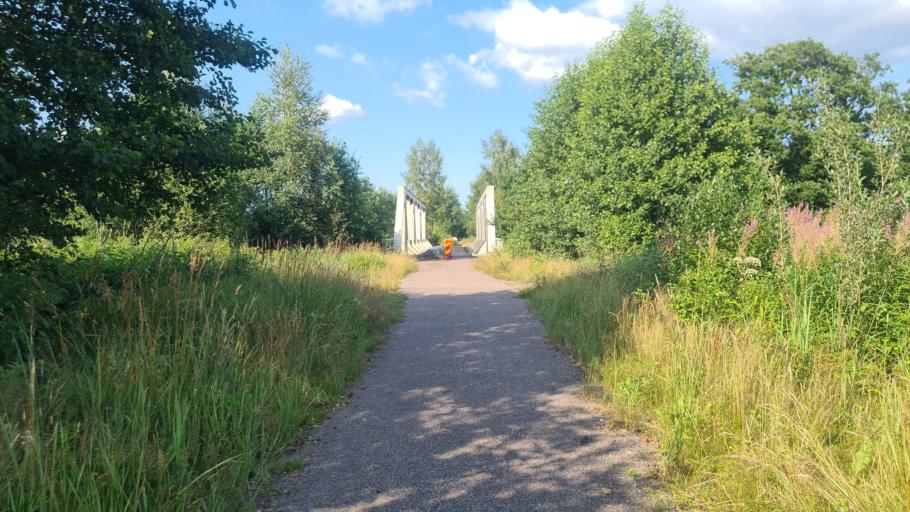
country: SE
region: Kronoberg
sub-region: Ljungby Kommun
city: Ljungby
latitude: 56.7928
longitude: 13.9071
